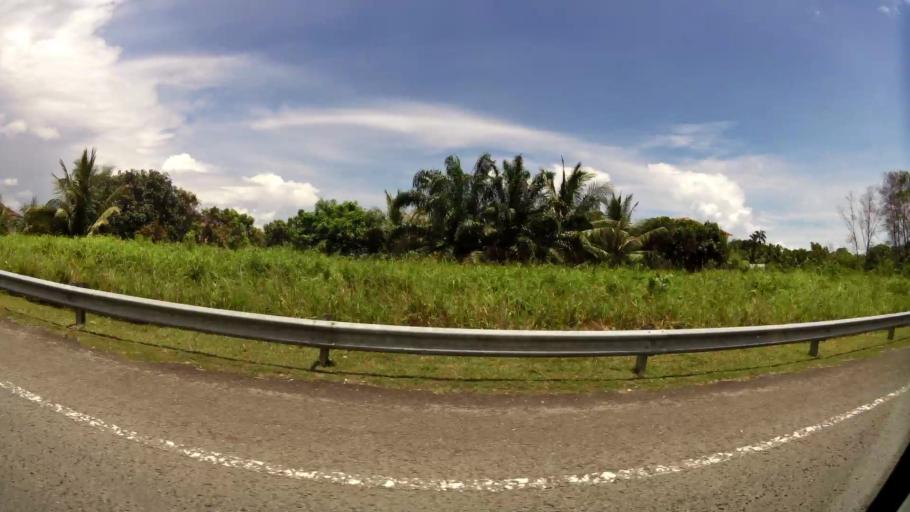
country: BN
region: Brunei and Muara
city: Bandar Seri Begawan
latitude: 4.9437
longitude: 114.9070
